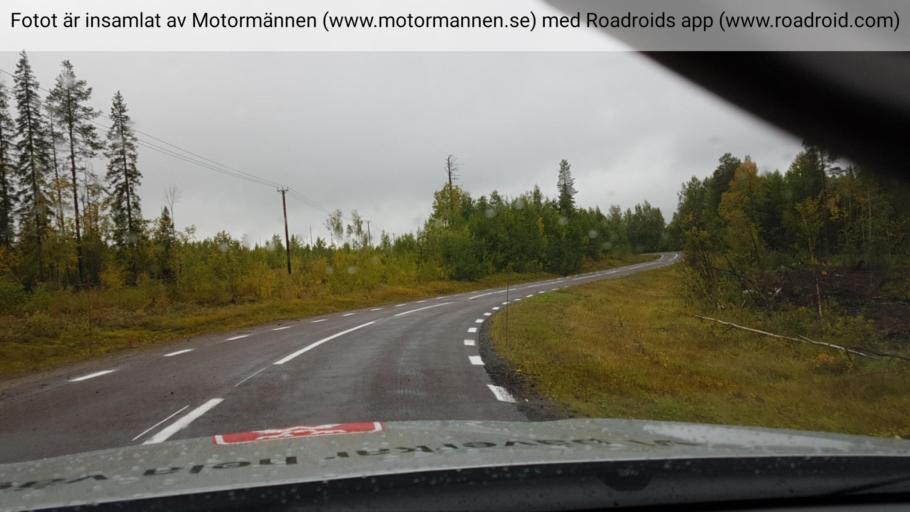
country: SE
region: Norrbotten
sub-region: Bodens Kommun
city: Boden
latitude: 66.1326
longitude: 21.2968
